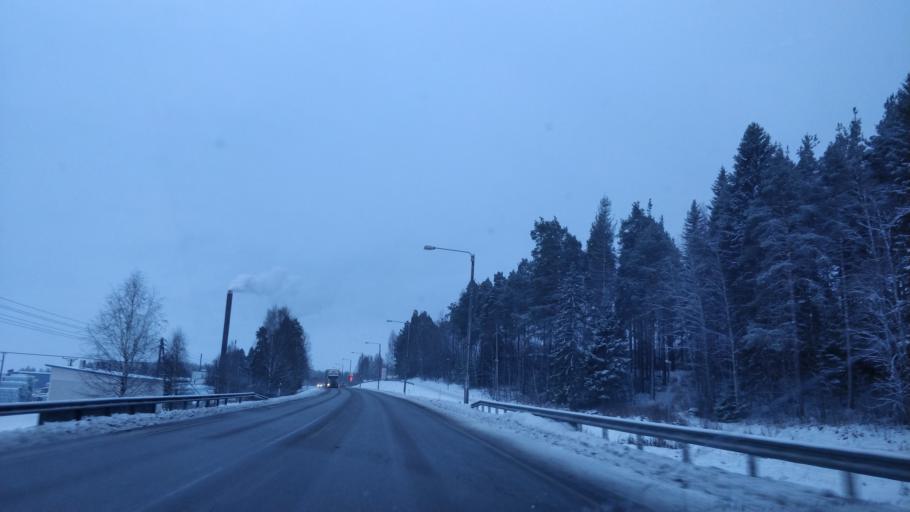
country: FI
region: Central Finland
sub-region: Saarijaervi-Viitasaari
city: Viitasaari
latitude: 63.0836
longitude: 25.8633
